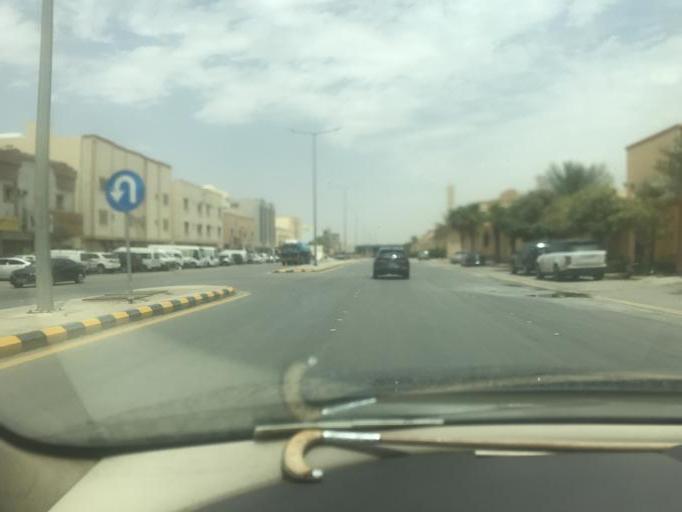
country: SA
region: Ar Riyad
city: Riyadh
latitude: 24.7962
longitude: 46.7054
